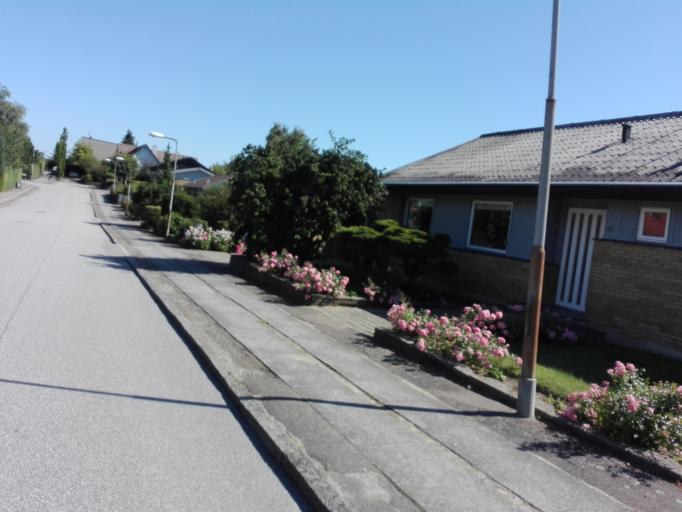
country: DK
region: Central Jutland
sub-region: Arhus Kommune
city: Tranbjerg
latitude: 56.1094
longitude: 10.1463
